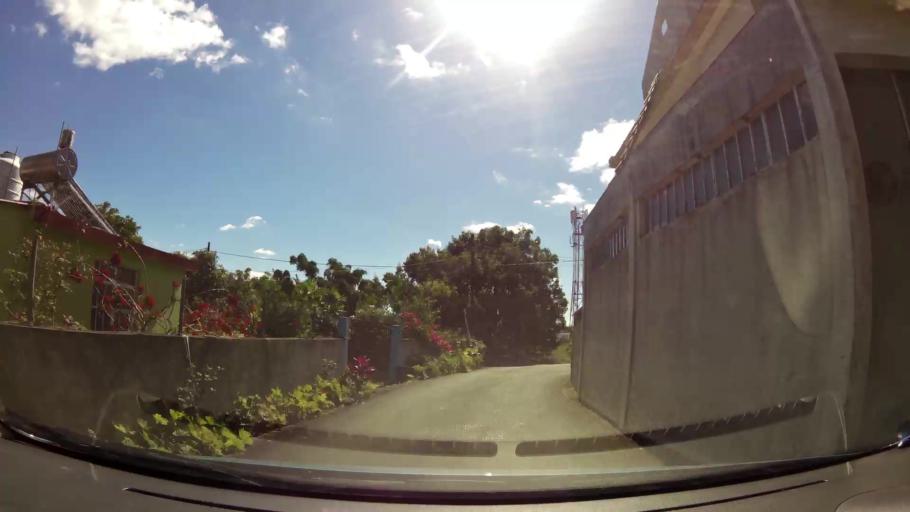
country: MU
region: Plaines Wilhems
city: Vacoas
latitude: -20.3090
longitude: 57.4751
